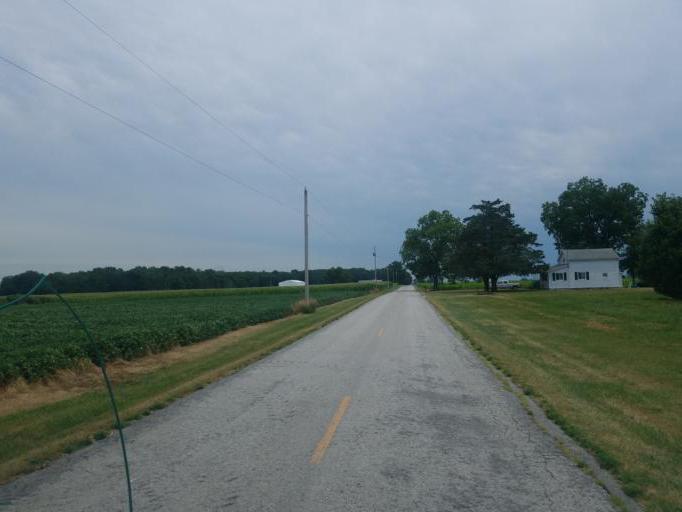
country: US
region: Ohio
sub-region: Defiance County
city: Hicksville
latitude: 41.2372
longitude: -84.7796
